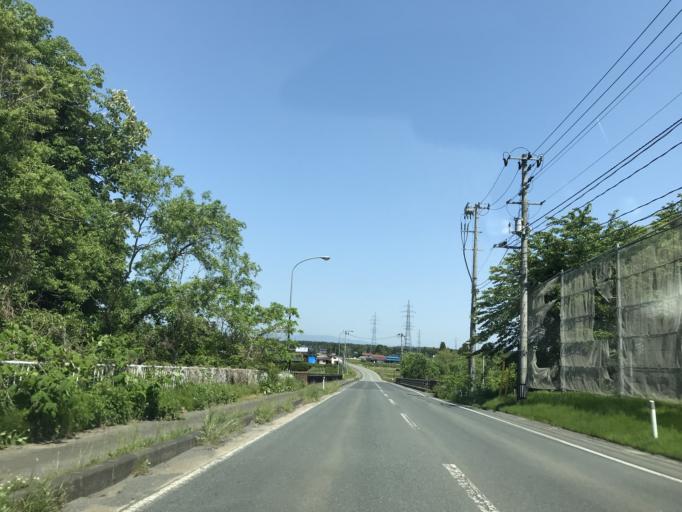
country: JP
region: Iwate
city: Mizusawa
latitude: 39.1744
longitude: 141.0822
